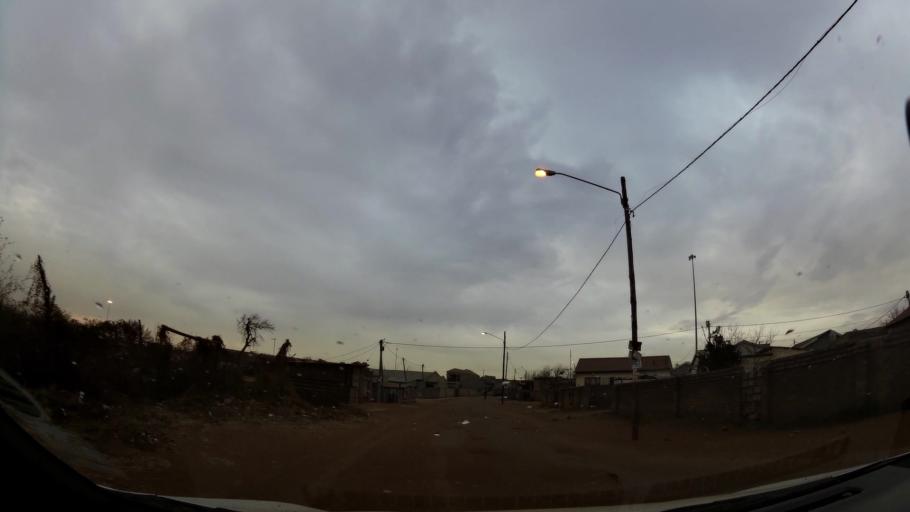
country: ZA
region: Gauteng
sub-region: Ekurhuleni Metropolitan Municipality
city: Germiston
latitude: -26.3826
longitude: 28.1723
